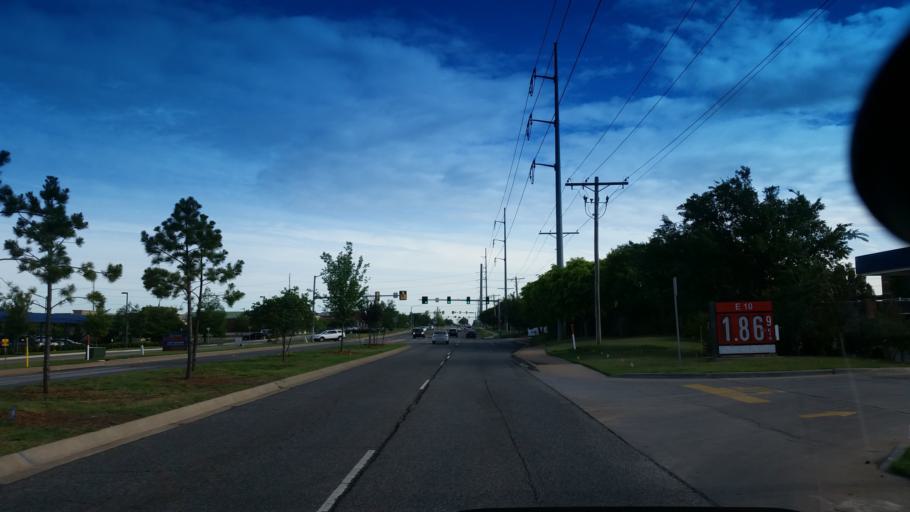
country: US
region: Oklahoma
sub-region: Oklahoma County
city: Edmond
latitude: 35.6644
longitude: -97.5140
